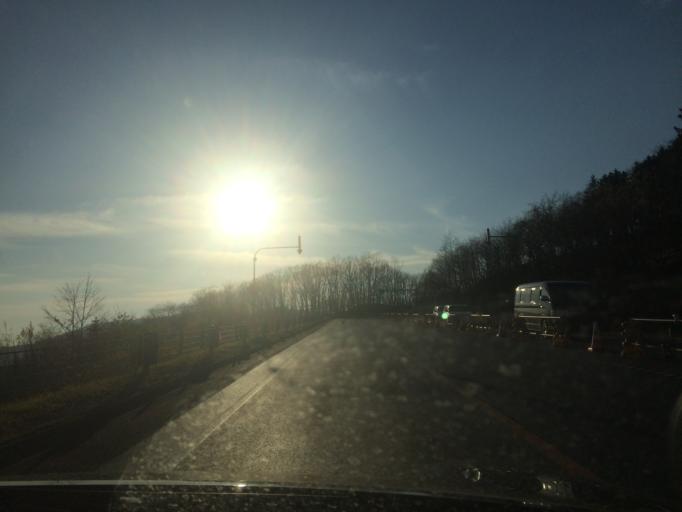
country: JP
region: Hokkaido
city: Otofuke
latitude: 42.9713
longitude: 142.8036
